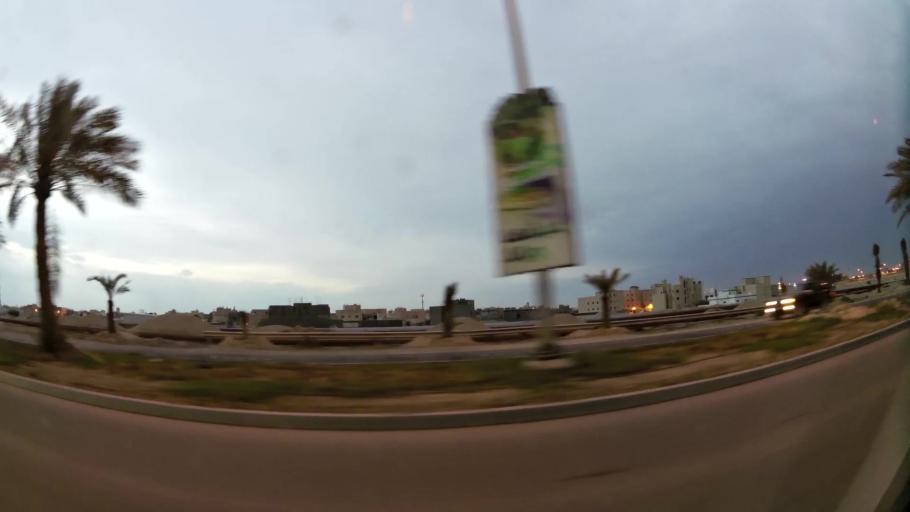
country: BH
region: Central Governorate
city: Madinat Hamad
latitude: 26.1417
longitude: 50.5035
